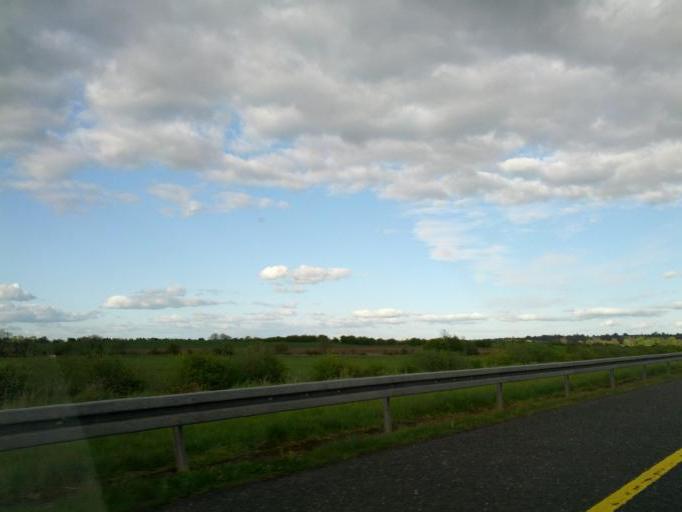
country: IE
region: Leinster
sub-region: An Mhi
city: Enfield
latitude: 53.4043
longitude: -6.8177
